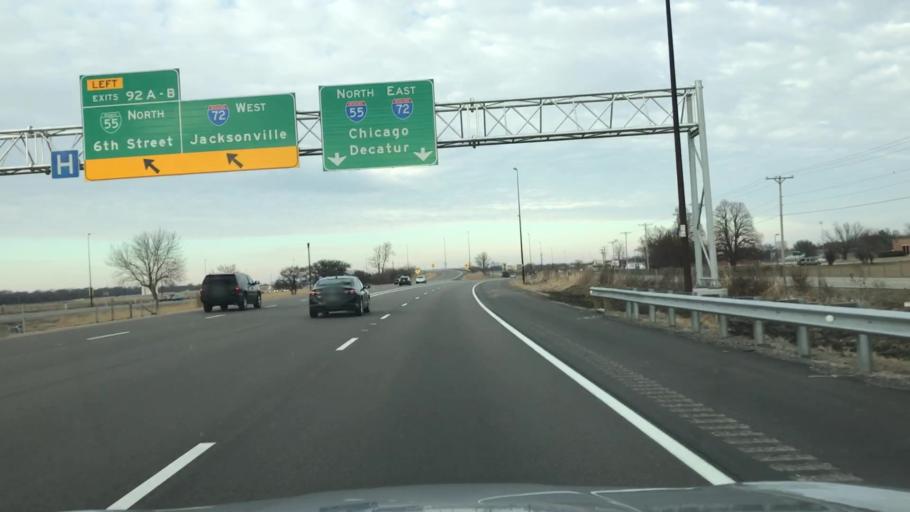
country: US
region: Illinois
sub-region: Sangamon County
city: Southern View
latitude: 39.7341
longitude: -89.6440
